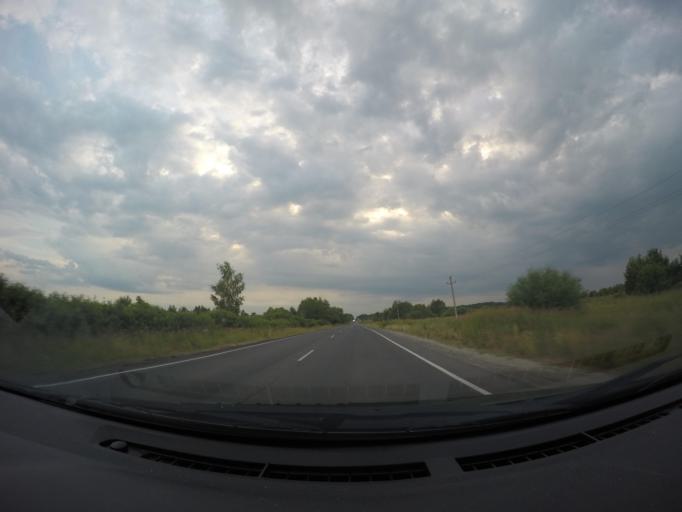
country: RU
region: Moskovskaya
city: Krasnyy Tkach
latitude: 55.4283
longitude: 39.2241
